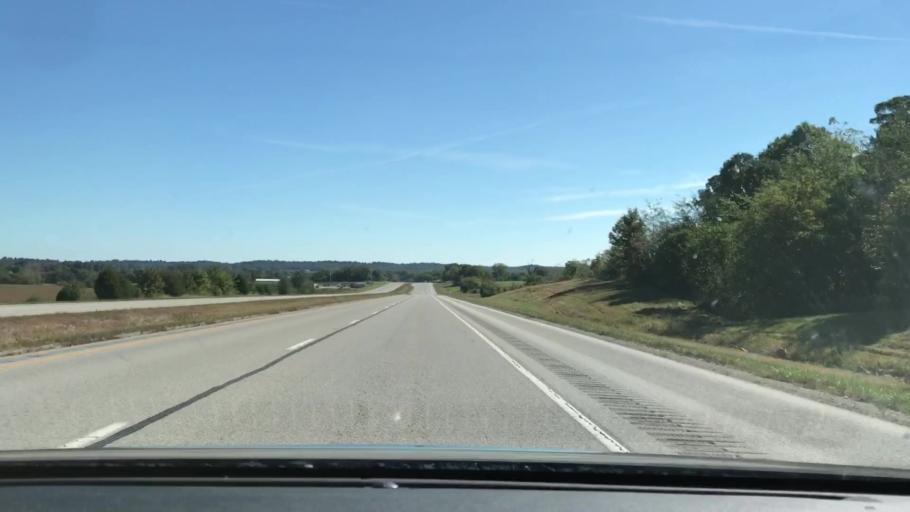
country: US
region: Kentucky
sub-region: Todd County
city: Elkton
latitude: 36.8210
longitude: -87.1838
